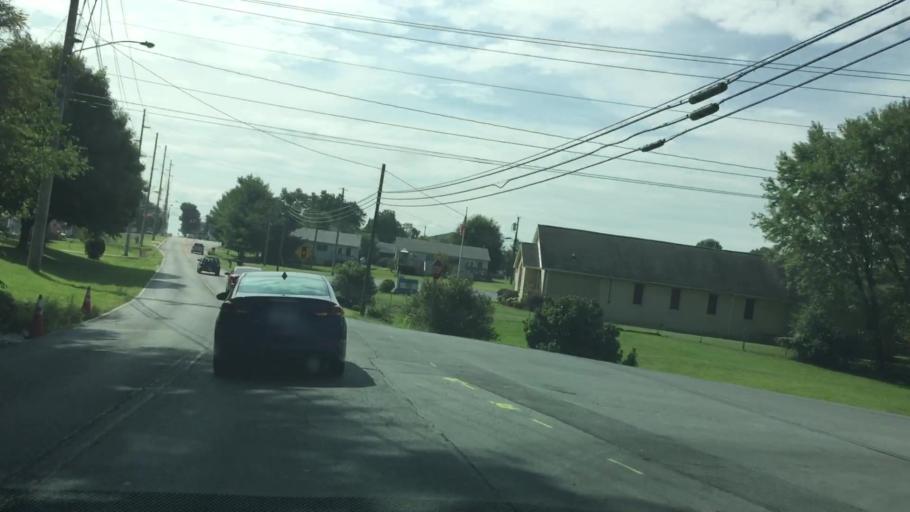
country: US
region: Tennessee
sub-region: Sullivan County
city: Fairmount
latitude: 36.6094
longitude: -82.1358
